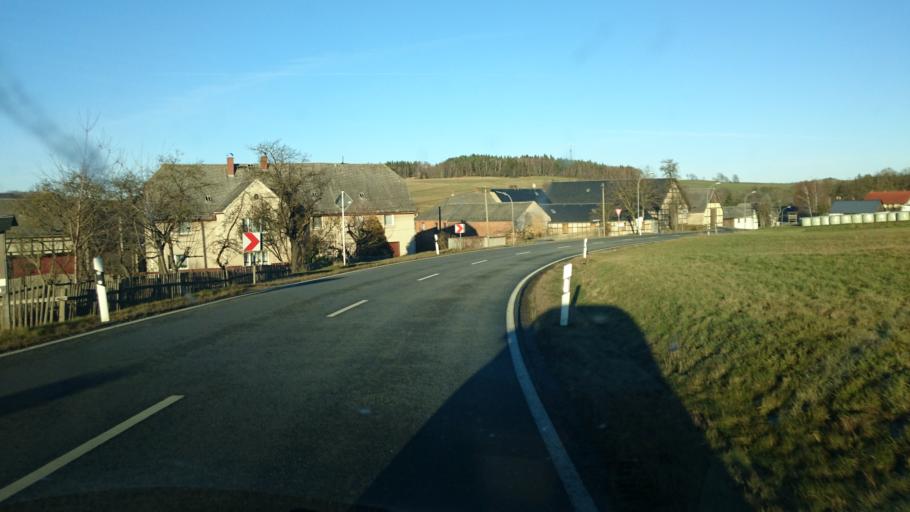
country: DE
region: Thuringia
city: Kirschkau
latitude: 50.6153
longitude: 11.9185
